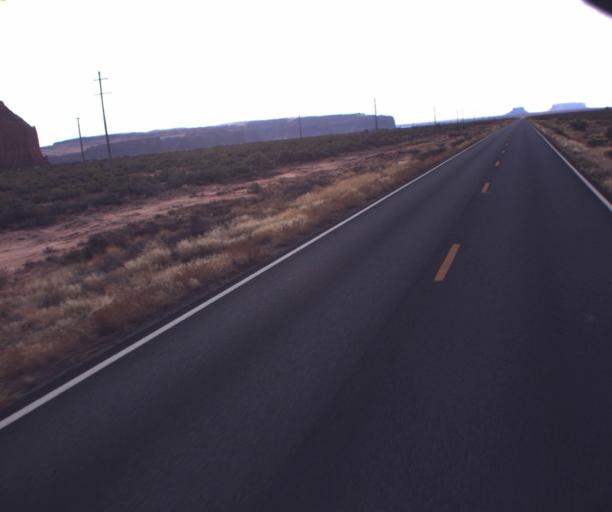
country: US
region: Arizona
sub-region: Apache County
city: Many Farms
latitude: 36.6665
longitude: -109.5977
